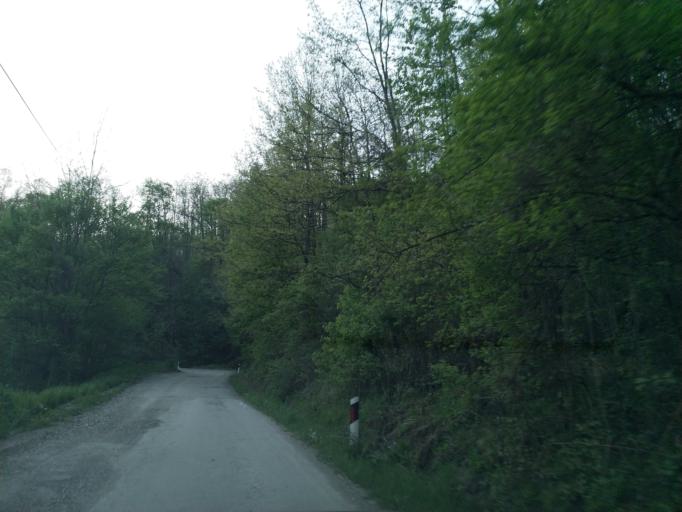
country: RS
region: Central Serbia
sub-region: Pomoravski Okrug
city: Despotovac
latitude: 43.9585
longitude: 21.5662
